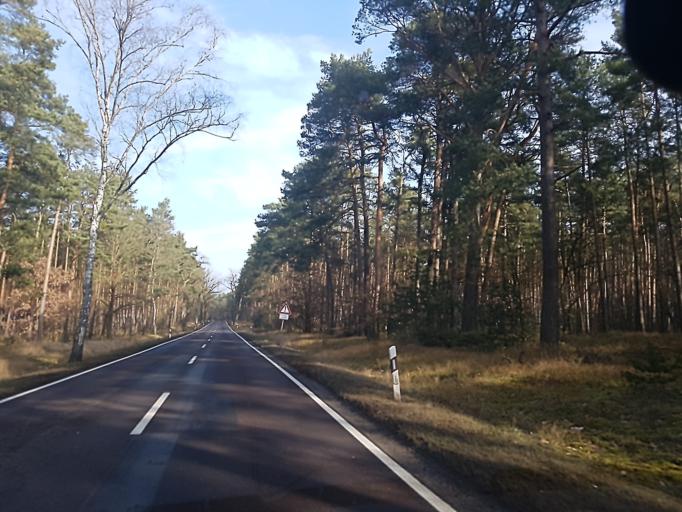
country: DE
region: Brandenburg
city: Wenzlow
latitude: 52.3333
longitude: 12.4936
